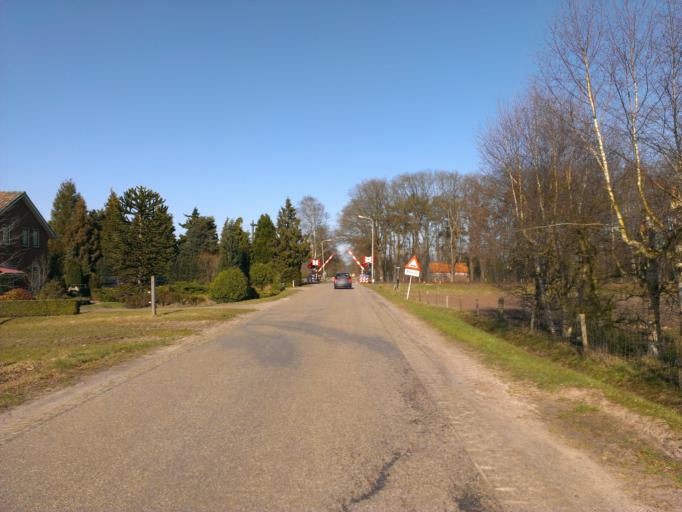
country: NL
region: Overijssel
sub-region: Gemeente Almelo
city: Almelo
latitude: 52.3263
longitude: 6.6947
